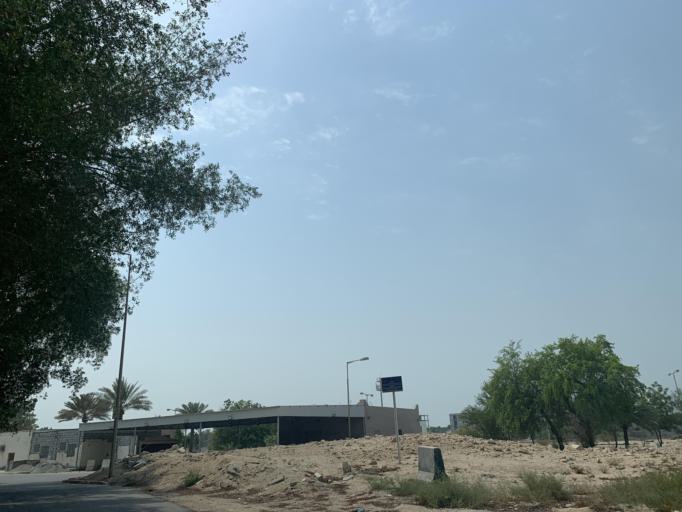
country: BH
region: Manama
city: Jidd Hafs
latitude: 26.2138
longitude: 50.4837
